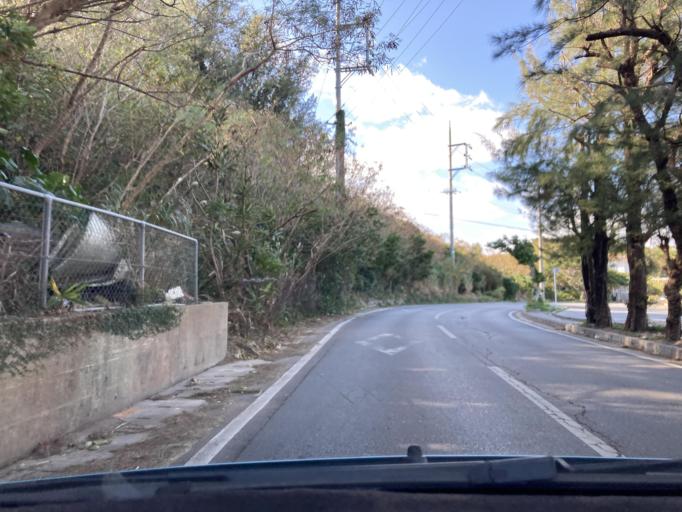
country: JP
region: Okinawa
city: Katsuren-haebaru
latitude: 26.3191
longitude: 127.9161
